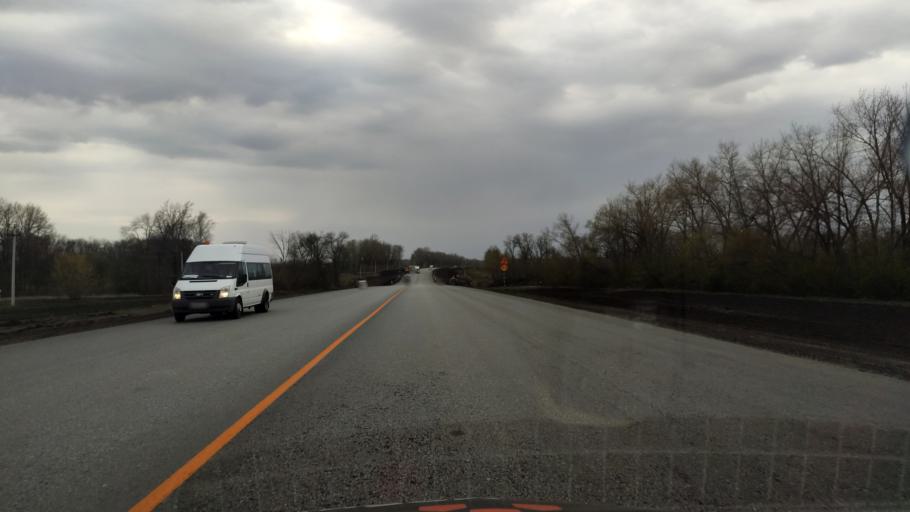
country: RU
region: Kursk
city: Gorshechnoye
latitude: 51.5472
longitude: 38.0722
